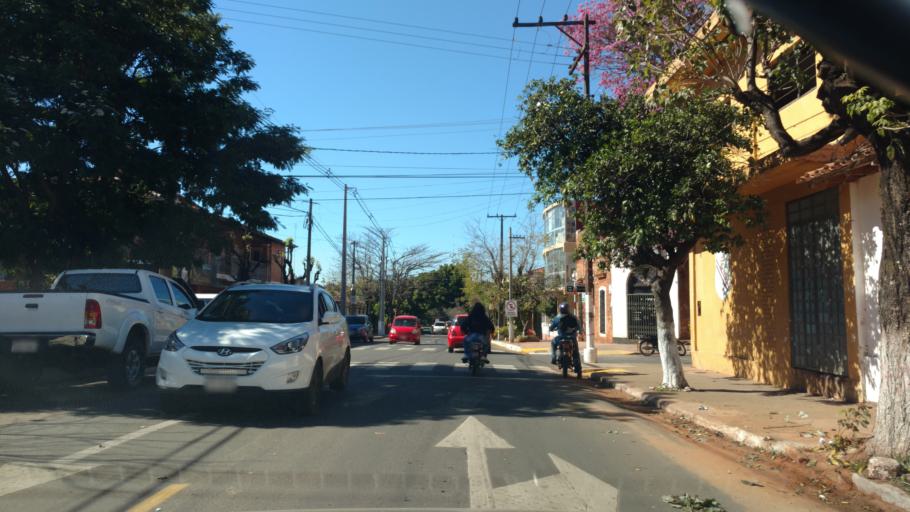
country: PY
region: Central
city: Itaugua
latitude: -25.3945
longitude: -57.3525
